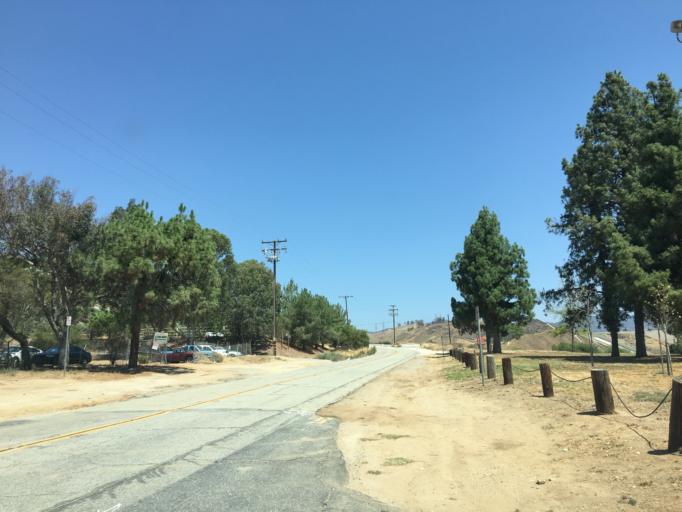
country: US
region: California
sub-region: Los Angeles County
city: Castaic
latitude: 34.5043
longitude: -118.6161
